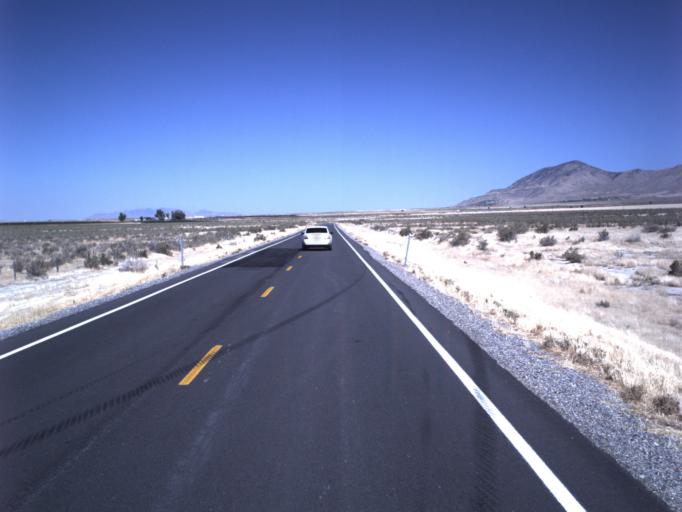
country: US
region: Utah
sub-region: Tooele County
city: Grantsville
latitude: 40.4758
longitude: -112.7459
